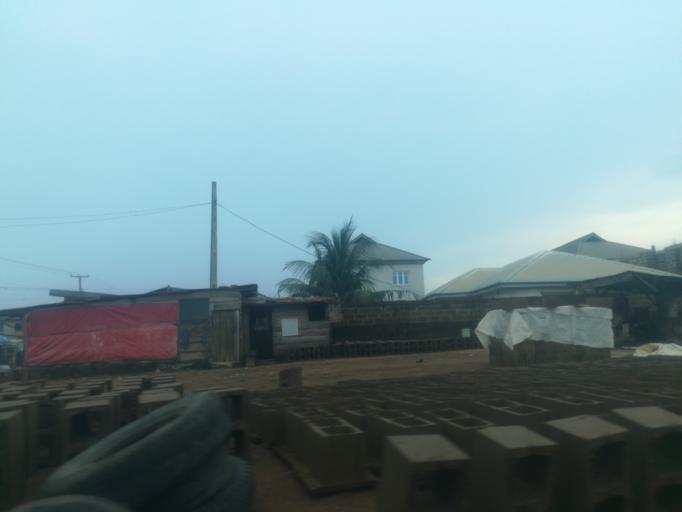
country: NG
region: Oyo
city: Ibadan
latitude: 7.3551
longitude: 3.8306
